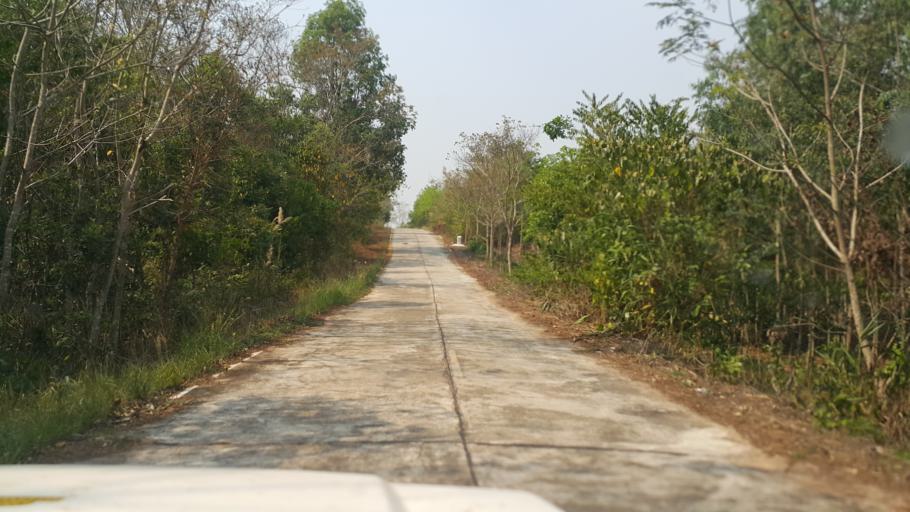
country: TH
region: Nakhon Phanom
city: Ban Phaeng
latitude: 17.9734
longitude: 104.1510
